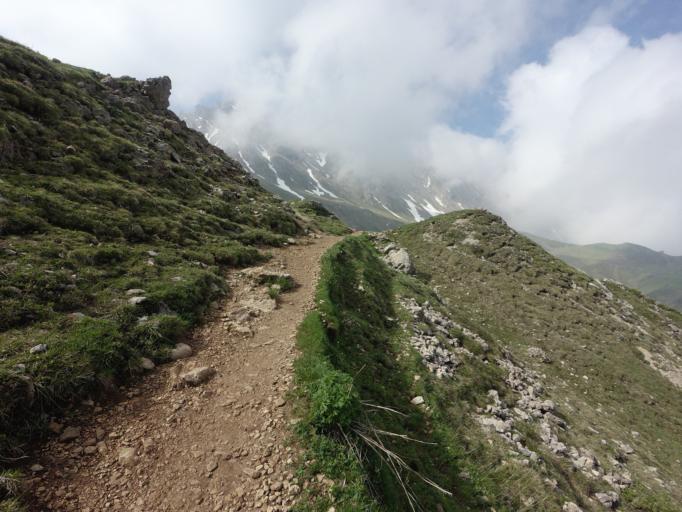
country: IT
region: Trentino-Alto Adige
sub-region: Bolzano
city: Ortisei
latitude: 46.5100
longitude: 11.6350
